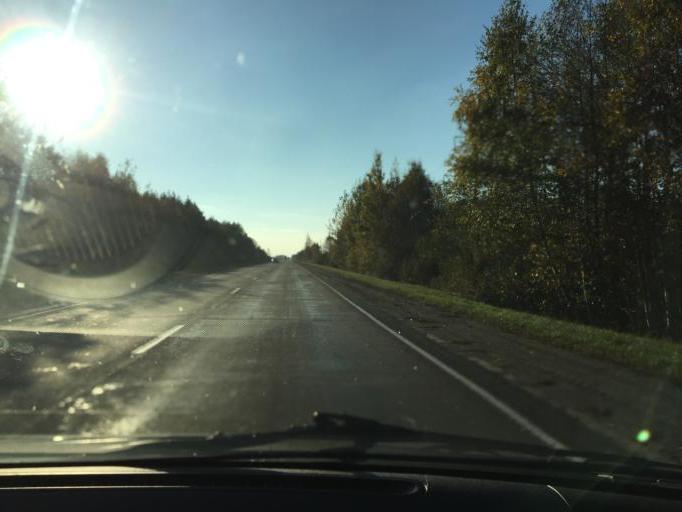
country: BY
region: Brest
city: Horad Luninyets
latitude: 52.3170
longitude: 26.5750
